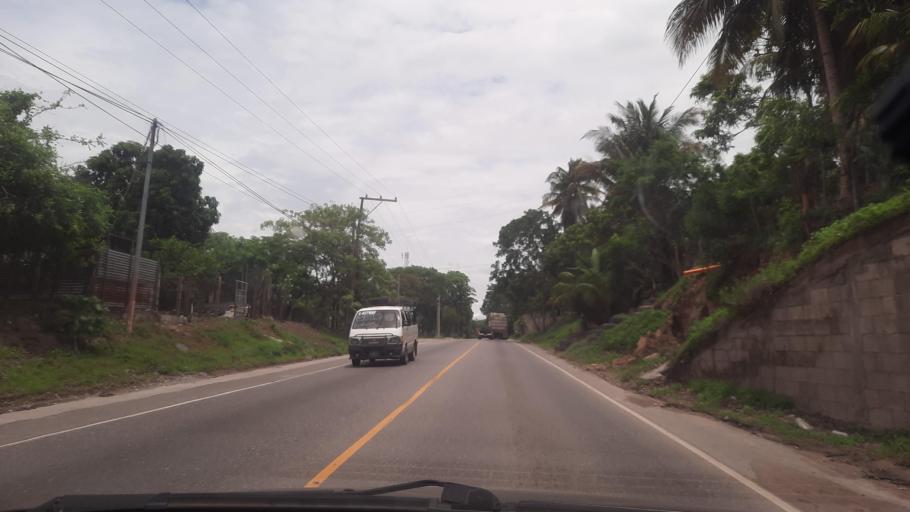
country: GT
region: Zacapa
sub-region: Municipio de Zacapa
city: Gualan
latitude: 15.0917
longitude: -89.4411
